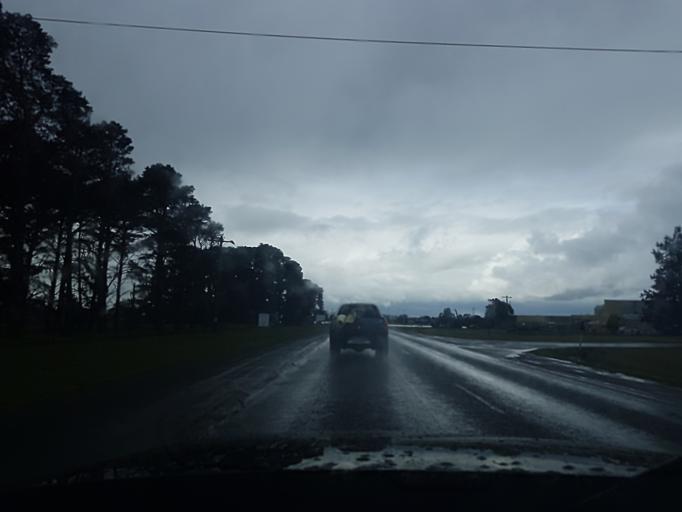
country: AU
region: Victoria
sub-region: Ballarat North
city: Newington
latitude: -37.5322
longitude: 143.8030
